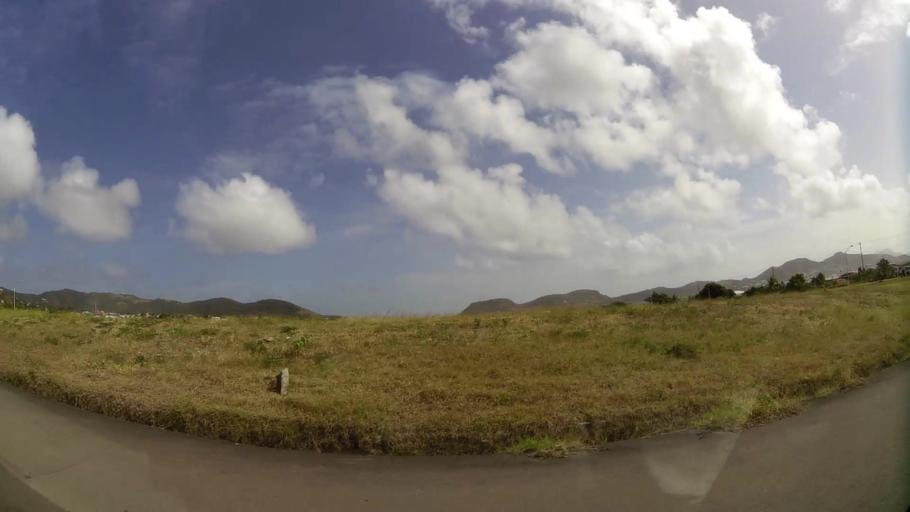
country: KN
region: Saint George Basseterre
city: Basseterre
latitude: 17.3034
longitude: -62.7312
